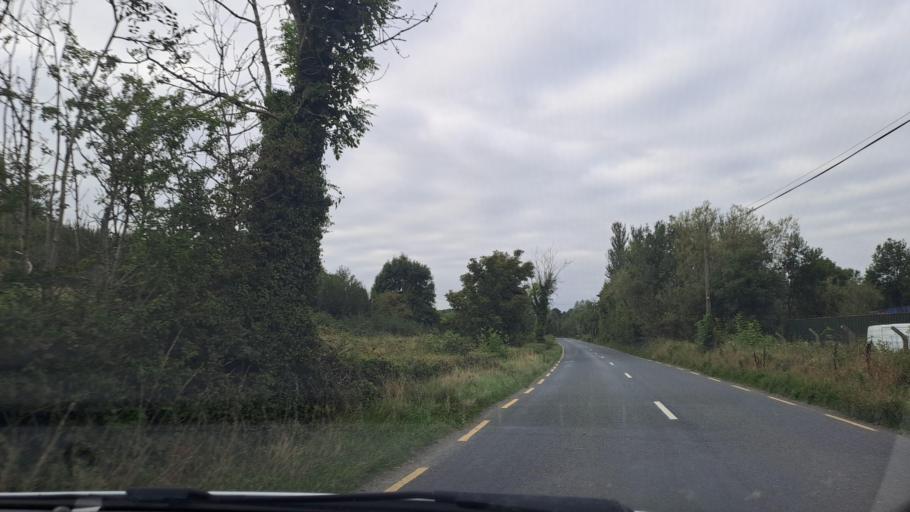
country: IE
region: Ulster
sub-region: County Monaghan
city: Carrickmacross
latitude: 54.0130
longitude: -6.7573
